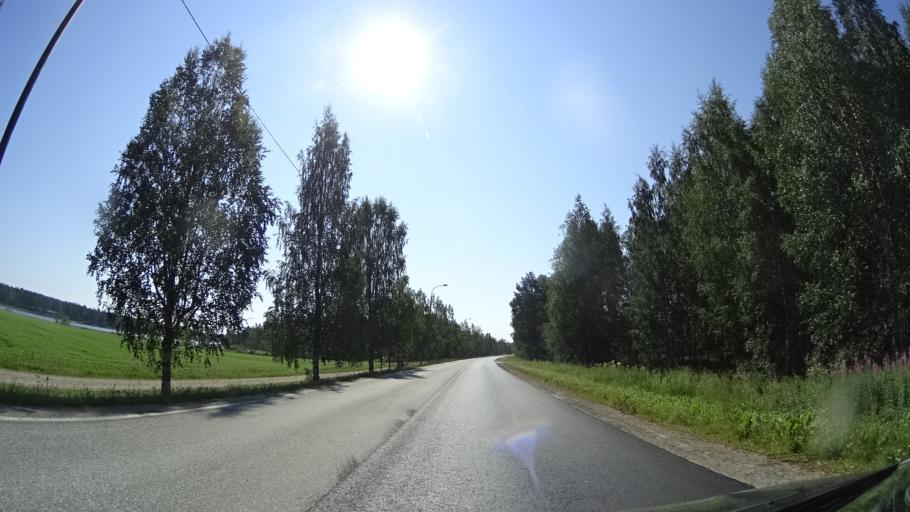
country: FI
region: North Karelia
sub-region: Joensuu
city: Juuka
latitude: 63.2443
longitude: 29.2736
